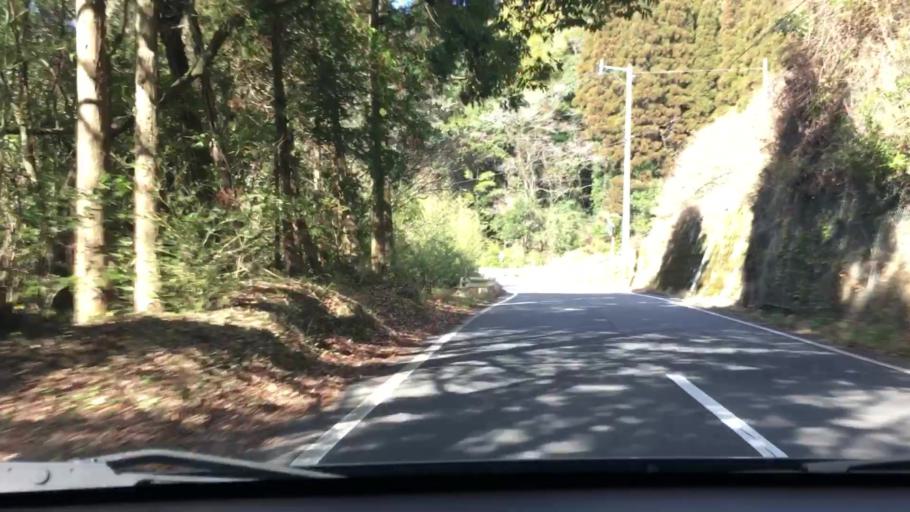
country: JP
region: Kagoshima
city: Ijuin
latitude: 31.7128
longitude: 130.4171
